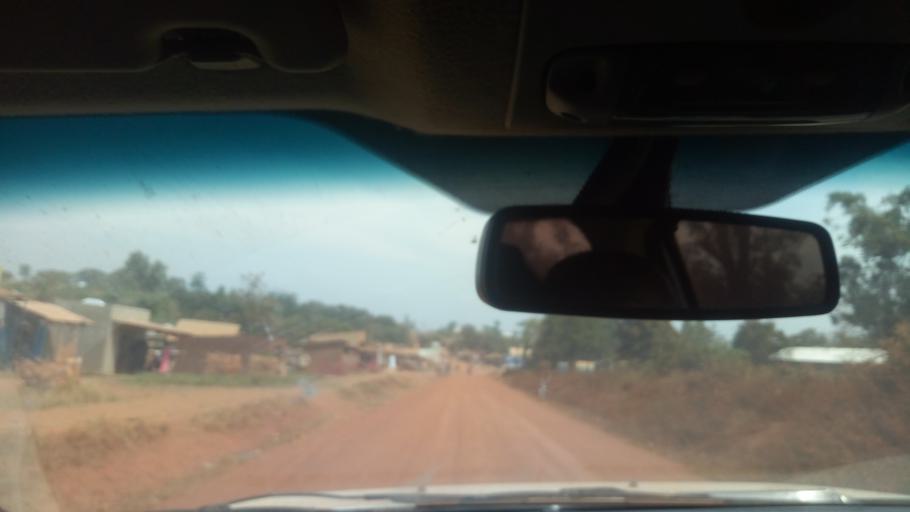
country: UG
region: Western Region
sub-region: Kiryandongo District
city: Kiryandongo
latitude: 1.9409
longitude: 32.1639
